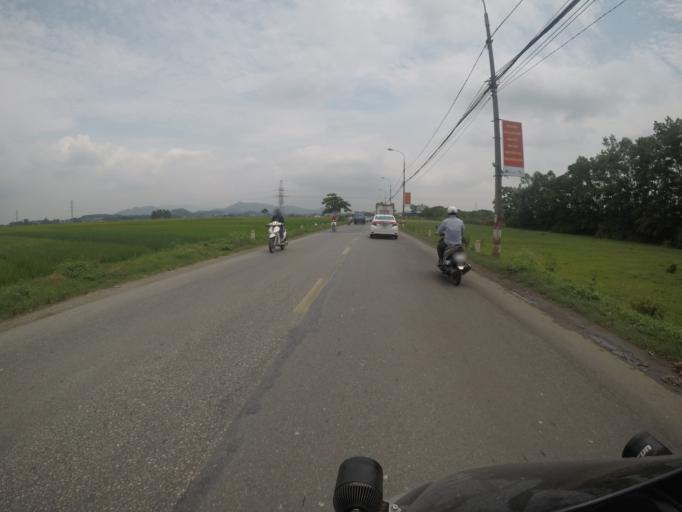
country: VN
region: Ha Noi
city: Soc Son
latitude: 21.2390
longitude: 105.8491
